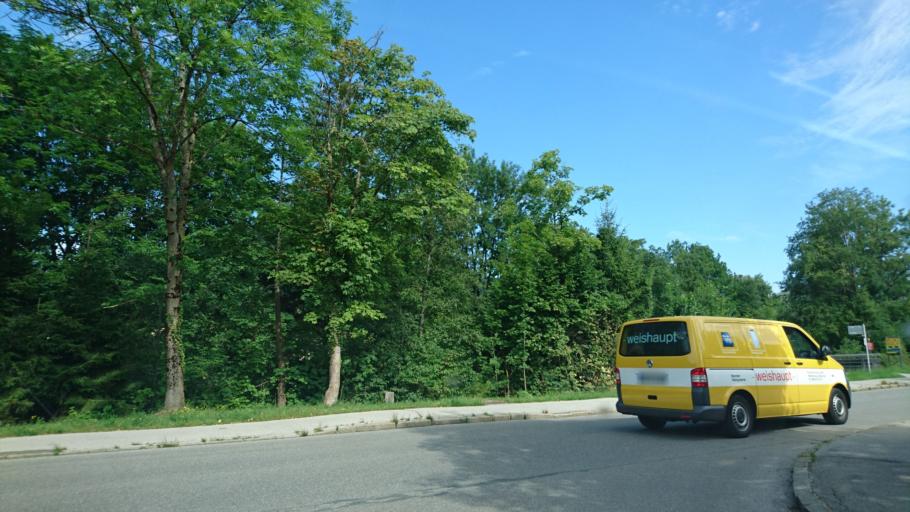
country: DE
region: Bavaria
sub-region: Upper Bavaria
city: Ruhpolding
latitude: 47.7573
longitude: 12.6488
